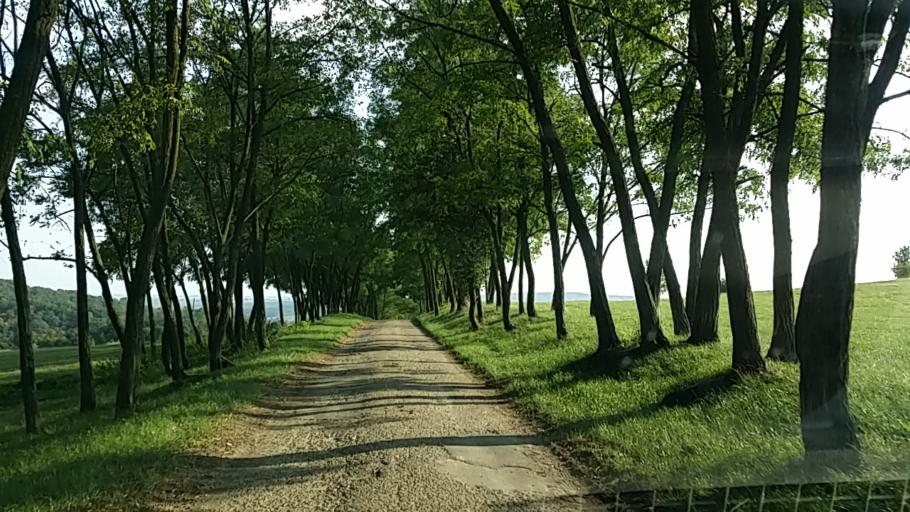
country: HU
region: Nograd
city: Bujak
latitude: 47.8771
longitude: 19.5004
